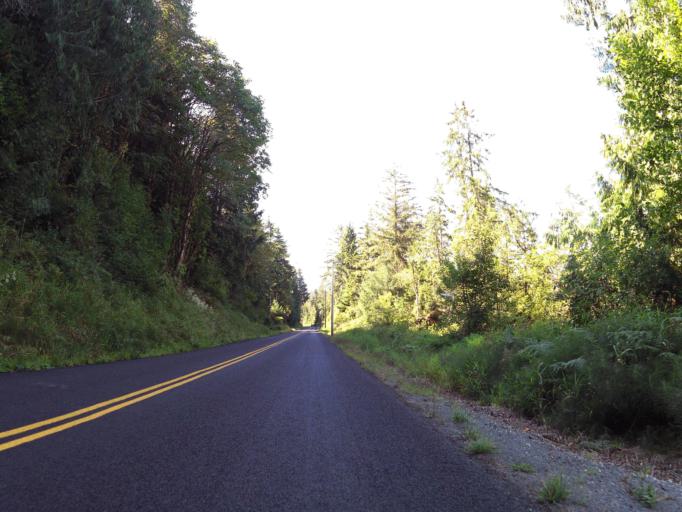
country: US
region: Washington
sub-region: Wahkiakum County
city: Cathlamet
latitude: 46.1926
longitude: -123.5746
